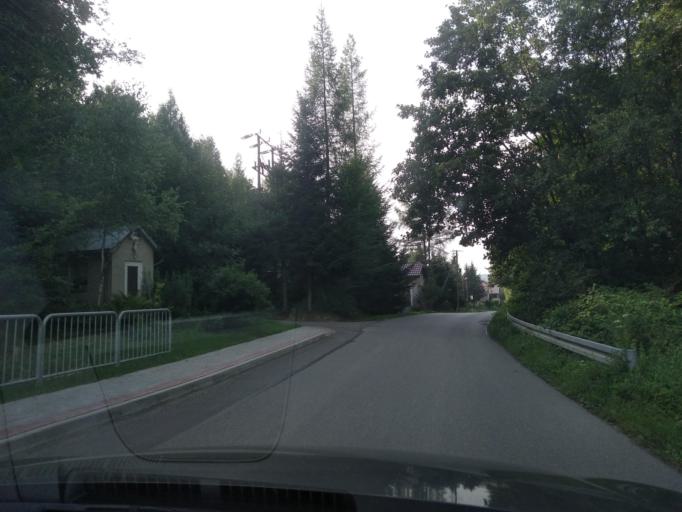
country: PL
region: Subcarpathian Voivodeship
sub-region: Powiat brzozowski
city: Dydnia
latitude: 49.6649
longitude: 22.1935
